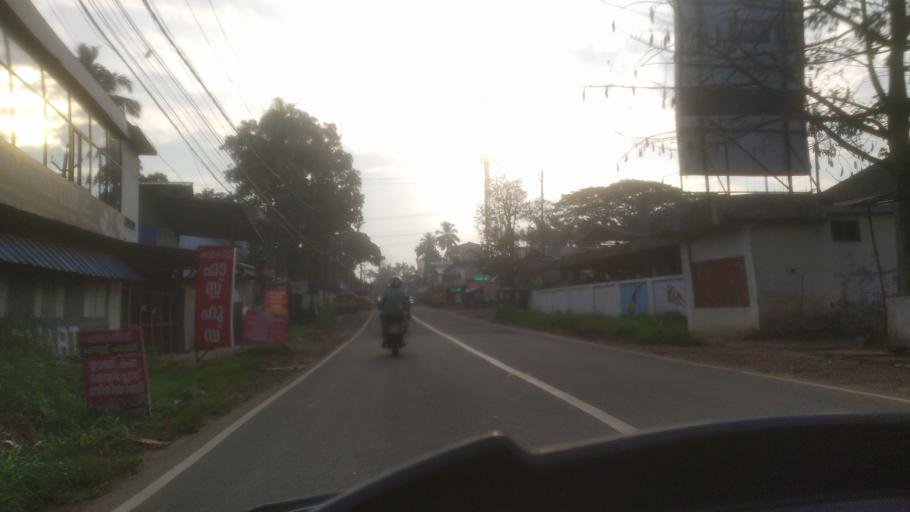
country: IN
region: Kerala
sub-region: Ernakulam
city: Perumpavur
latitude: 10.1164
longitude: 76.4459
